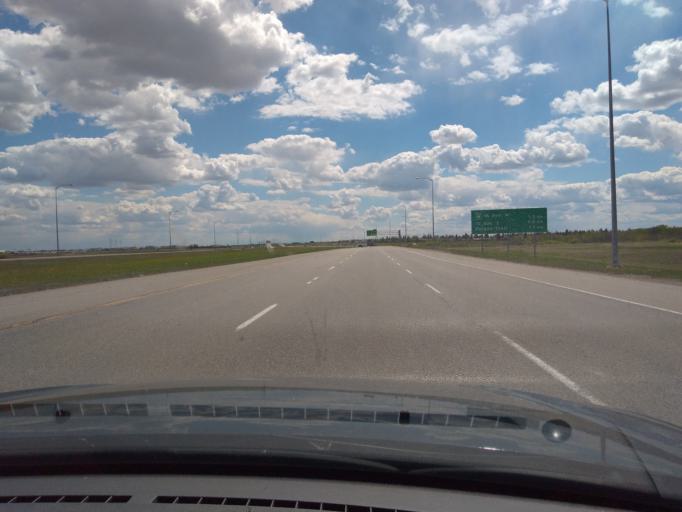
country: CA
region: Alberta
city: Chestermere
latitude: 51.0873
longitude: -113.9199
